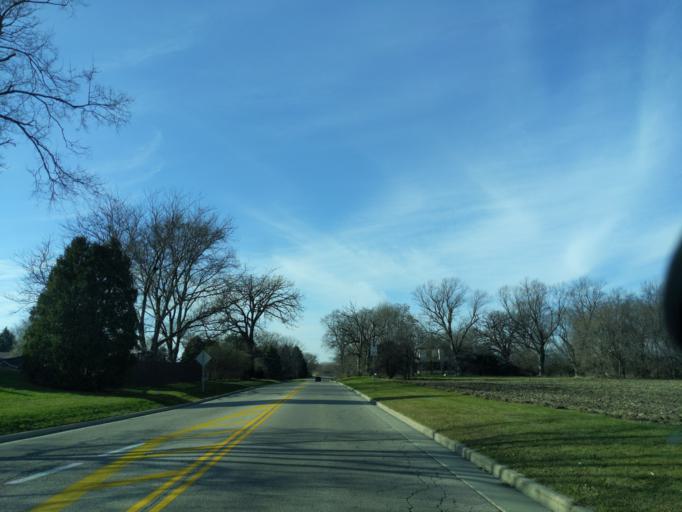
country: US
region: Wisconsin
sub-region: Walworth County
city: Elkhorn
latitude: 42.6845
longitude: -88.5471
